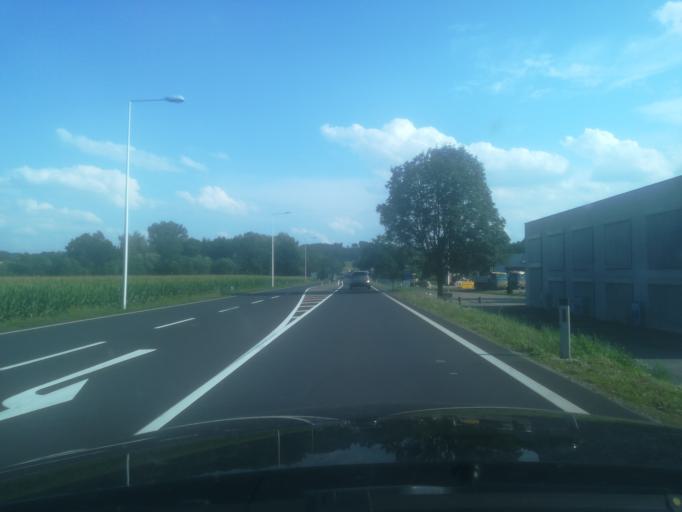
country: AT
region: Upper Austria
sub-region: Politischer Bezirk Grieskirchen
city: Bad Schallerbach
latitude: 48.2040
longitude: 13.9265
